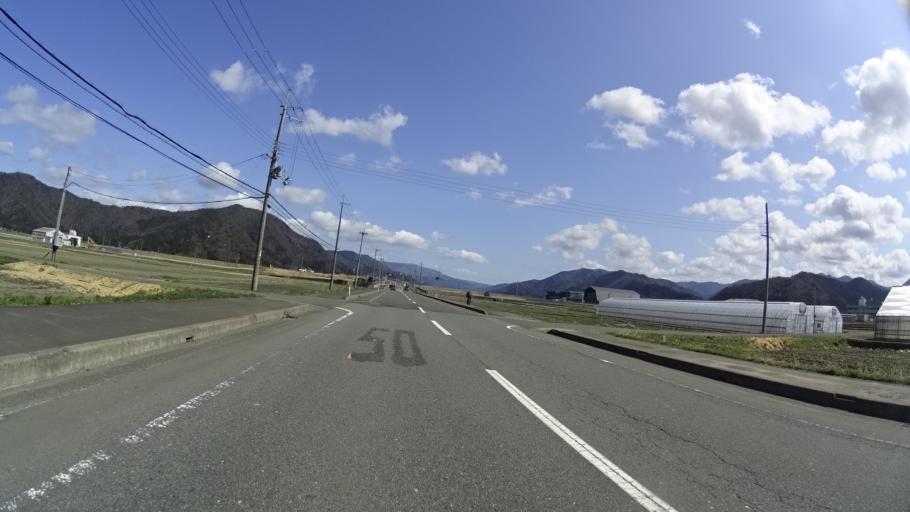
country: JP
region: Fukui
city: Obama
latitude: 35.4877
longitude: 135.7823
